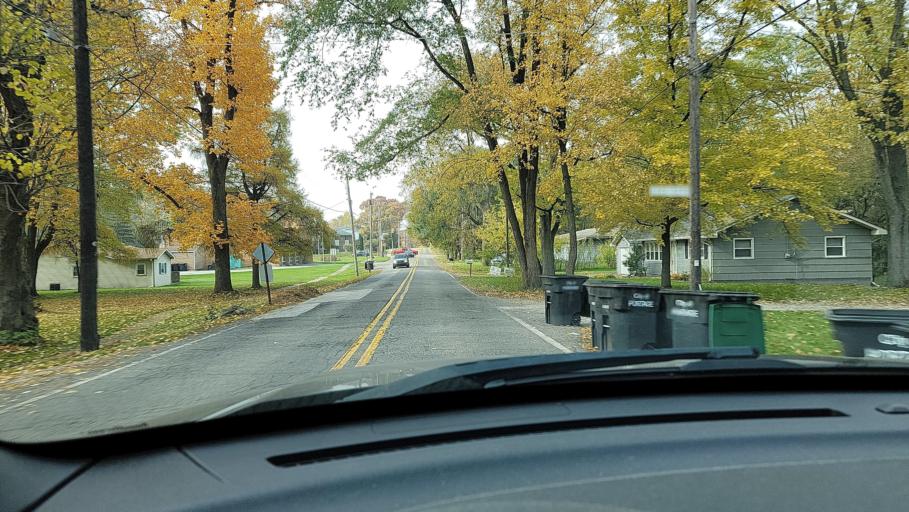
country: US
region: Indiana
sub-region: Porter County
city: Portage
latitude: 41.5941
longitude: -87.1718
